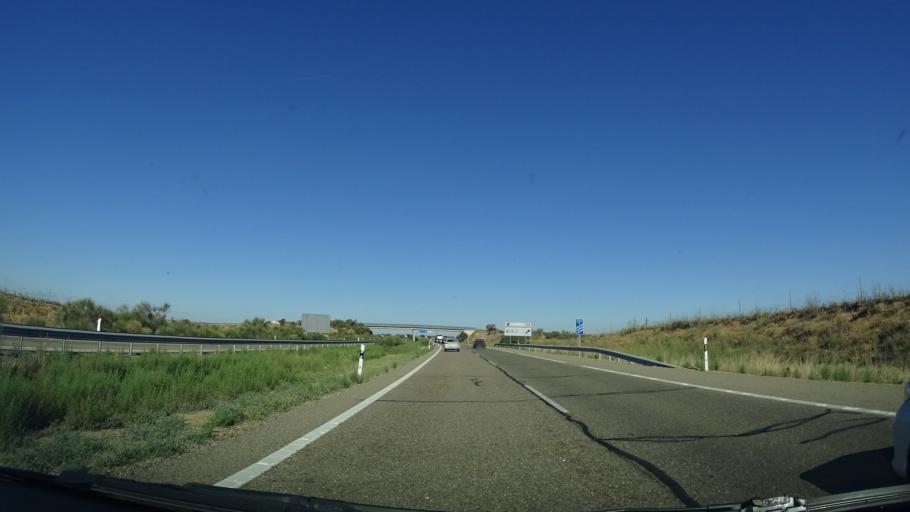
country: ES
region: Castille and Leon
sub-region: Provincia de Zamora
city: Villalpando
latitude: 41.8539
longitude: -5.4111
